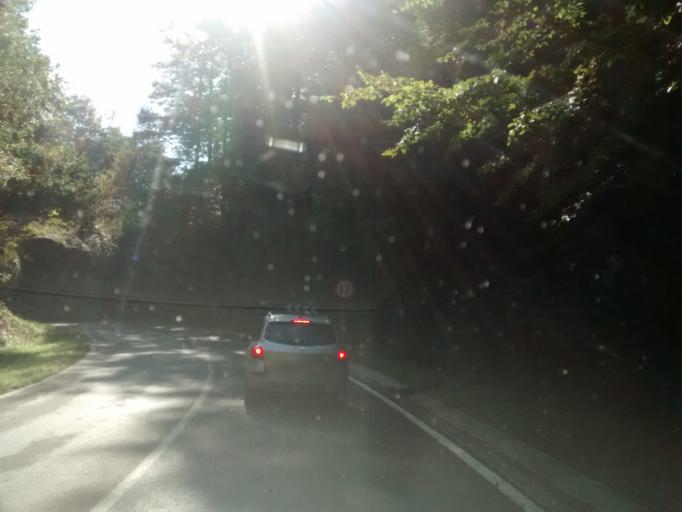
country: ES
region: Cantabria
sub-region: Provincia de Cantabria
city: Reinosa
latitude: 42.9596
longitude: -4.0590
